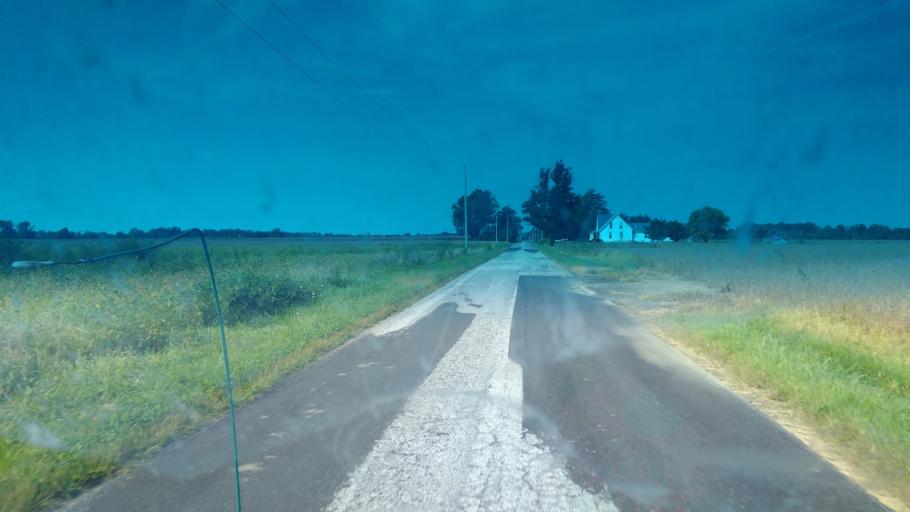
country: US
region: Ohio
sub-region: Morrow County
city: Mount Gilead
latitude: 40.6159
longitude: -82.9243
